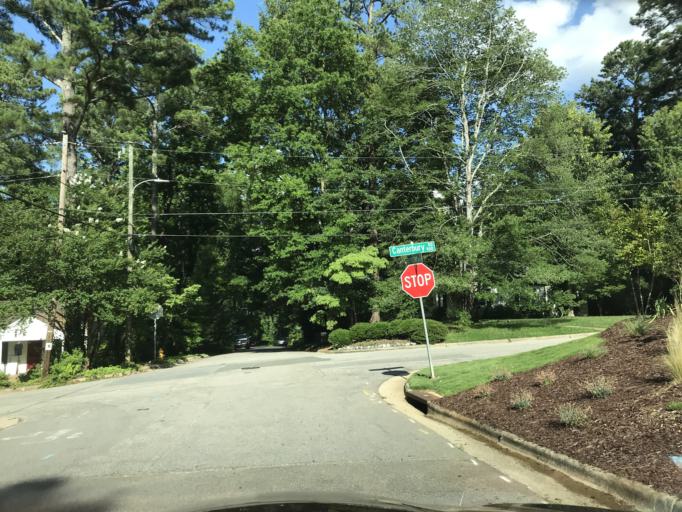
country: US
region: North Carolina
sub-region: Wake County
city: West Raleigh
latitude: 35.7985
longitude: -78.6694
